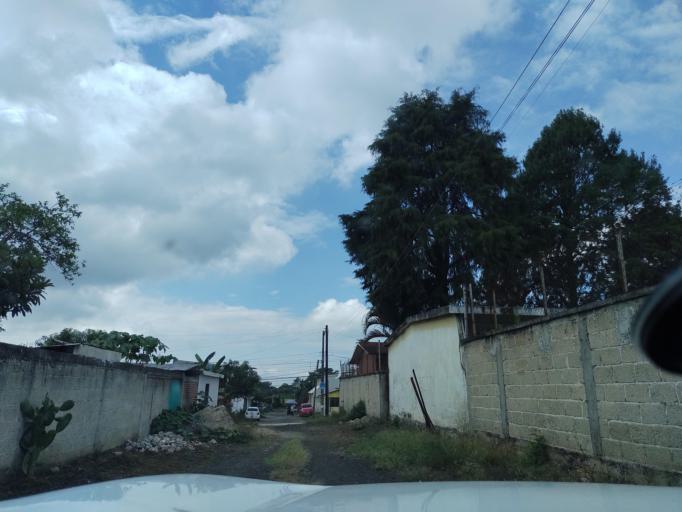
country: MX
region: Veracruz
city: Coatepec
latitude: 19.4824
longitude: -96.9343
